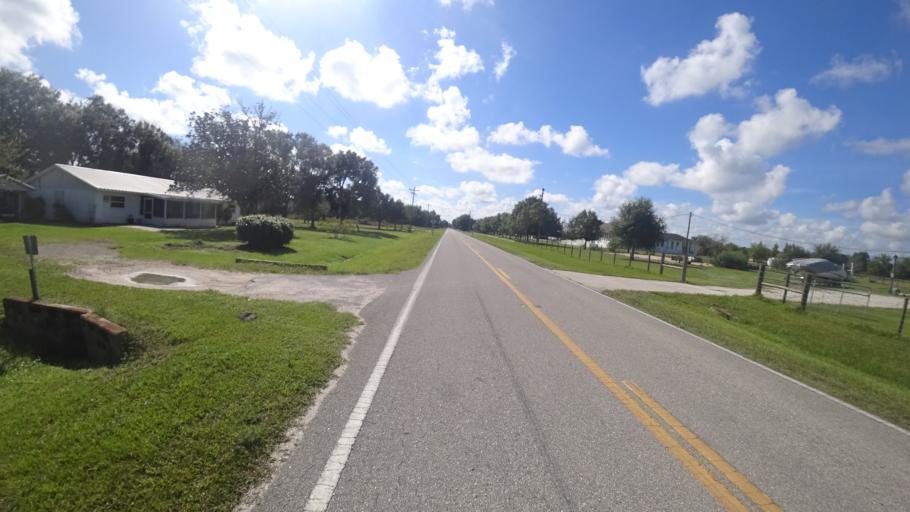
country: US
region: Florida
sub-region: Sarasota County
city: Lake Sarasota
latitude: 27.3600
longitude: -82.1625
